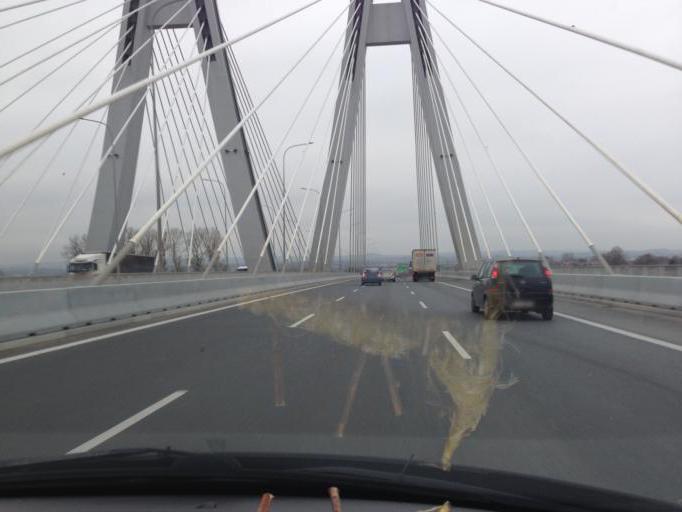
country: PL
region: Lesser Poland Voivodeship
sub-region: Powiat wielicki
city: Kokotow
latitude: 50.0512
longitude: 20.0725
